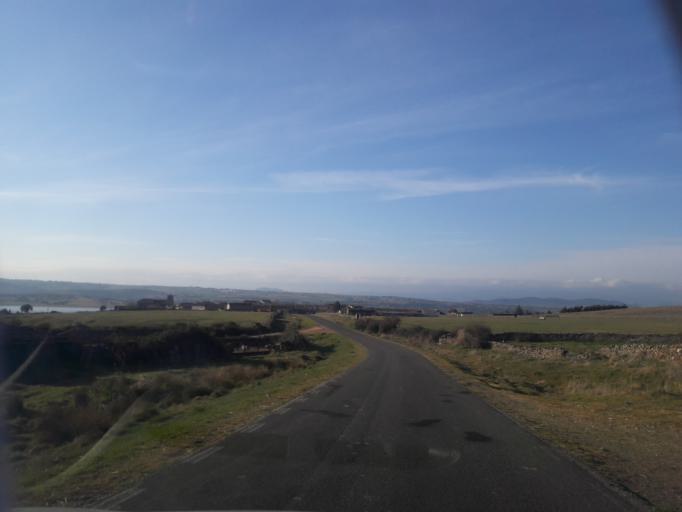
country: ES
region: Castille and Leon
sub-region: Provincia de Salamanca
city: Salvatierra de Tormes
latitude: 40.5946
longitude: -5.5993
